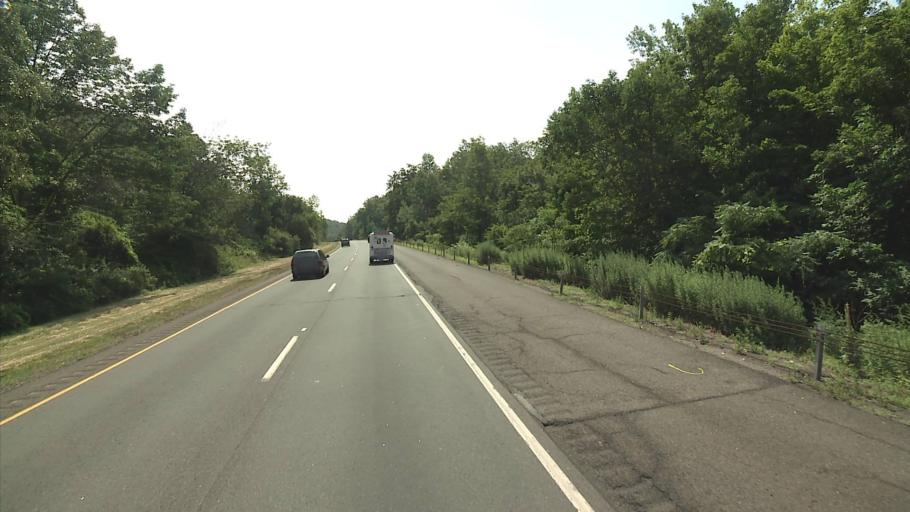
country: US
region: Connecticut
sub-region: New Haven County
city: Meriden
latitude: 41.5521
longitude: -72.8376
